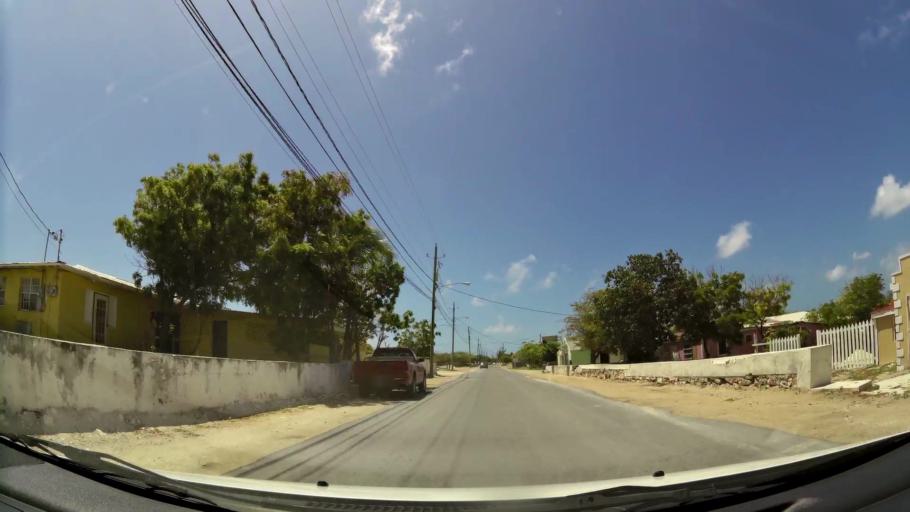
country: TC
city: Cockburn Town
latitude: 21.4775
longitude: -71.1453
